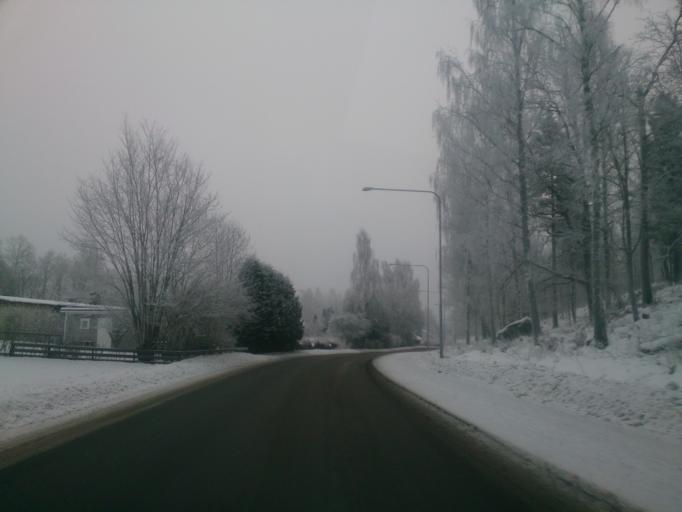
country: SE
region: OEstergoetland
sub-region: Atvidabergs Kommun
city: Atvidaberg
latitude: 58.1884
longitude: 16.0083
